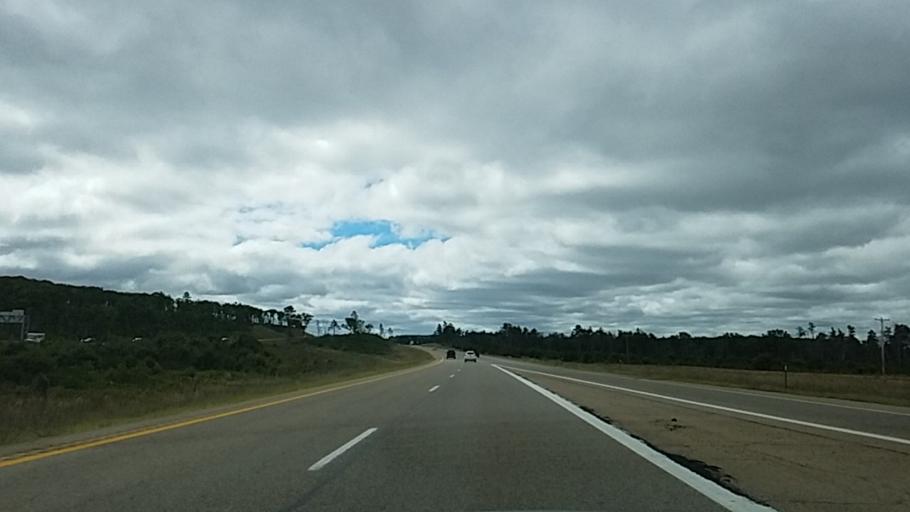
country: US
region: Michigan
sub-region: Crawford County
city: Grayling
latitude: 44.6431
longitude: -84.7084
